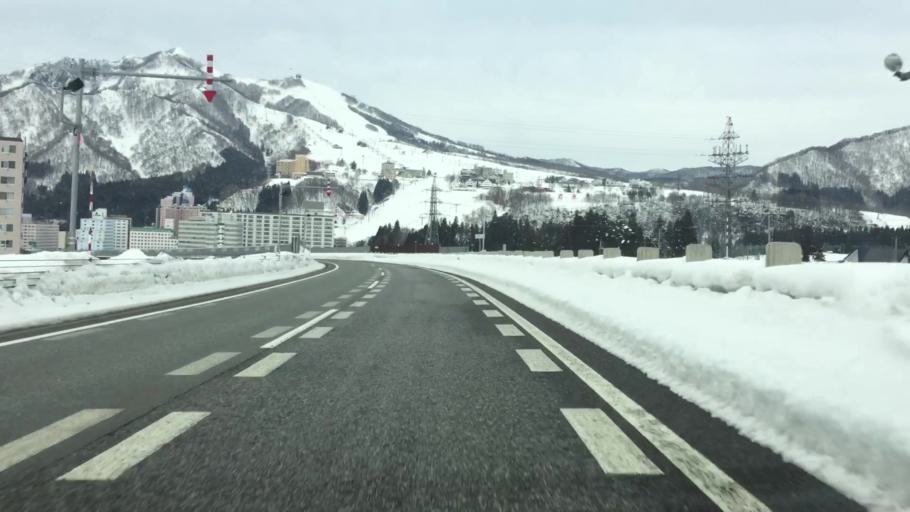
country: JP
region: Niigata
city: Shiozawa
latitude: 36.9233
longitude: 138.8415
